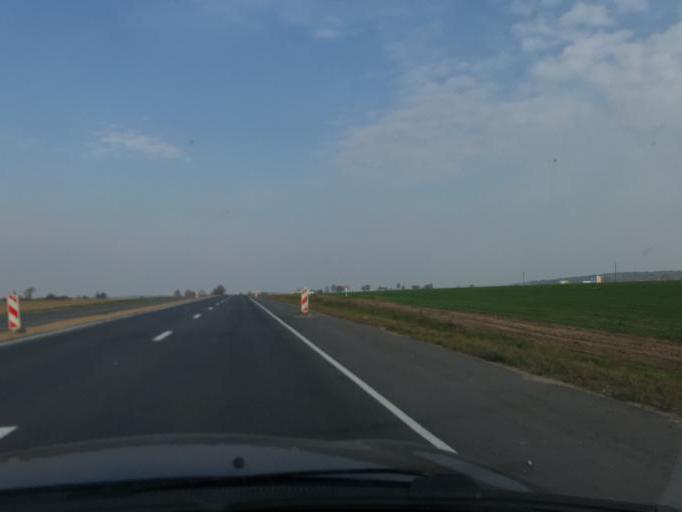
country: BY
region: Grodnenskaya
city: Shchuchin
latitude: 53.7211
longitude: 24.9639
